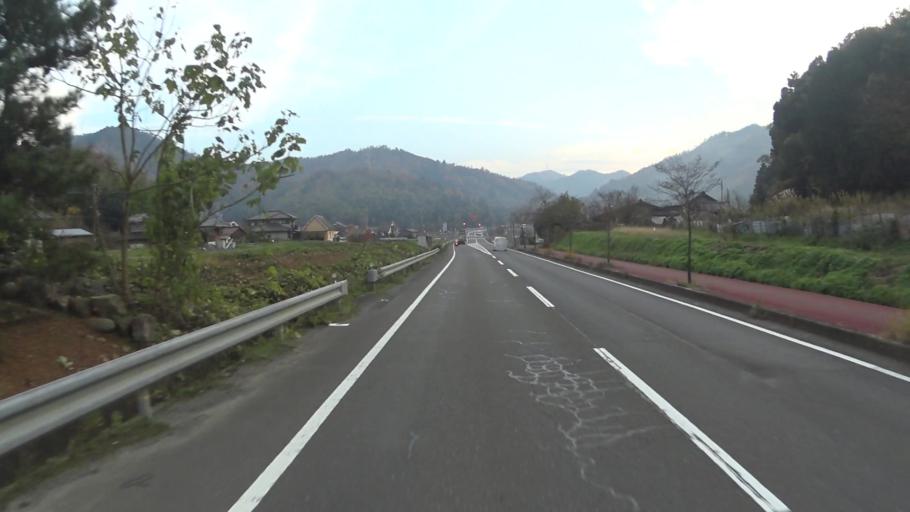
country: JP
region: Kyoto
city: Maizuru
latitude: 35.4665
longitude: 135.4233
